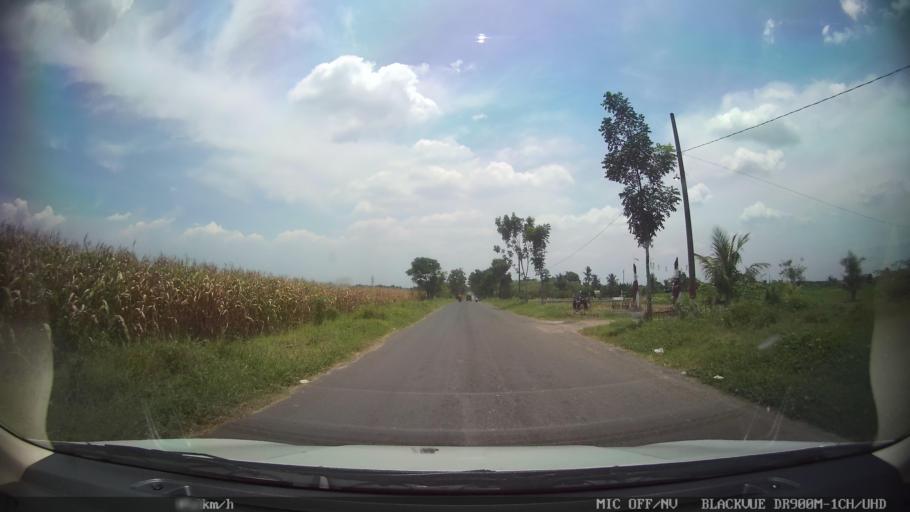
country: ID
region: North Sumatra
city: Binjai
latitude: 3.5912
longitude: 98.5210
